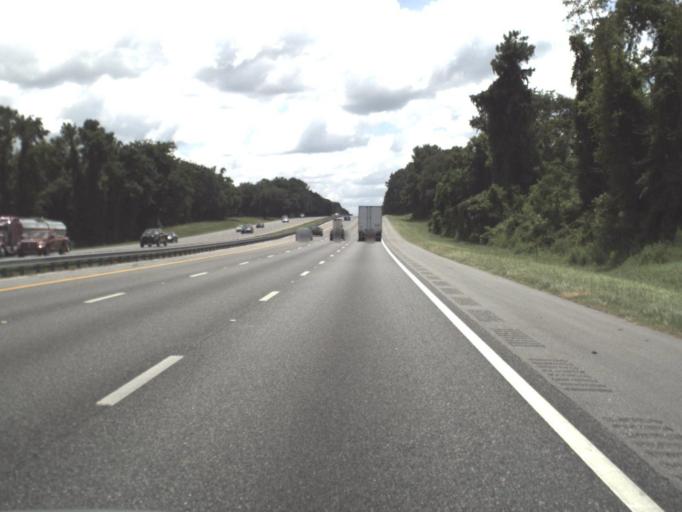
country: US
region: Florida
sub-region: Alachua County
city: High Springs
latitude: 29.9626
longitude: -82.5726
